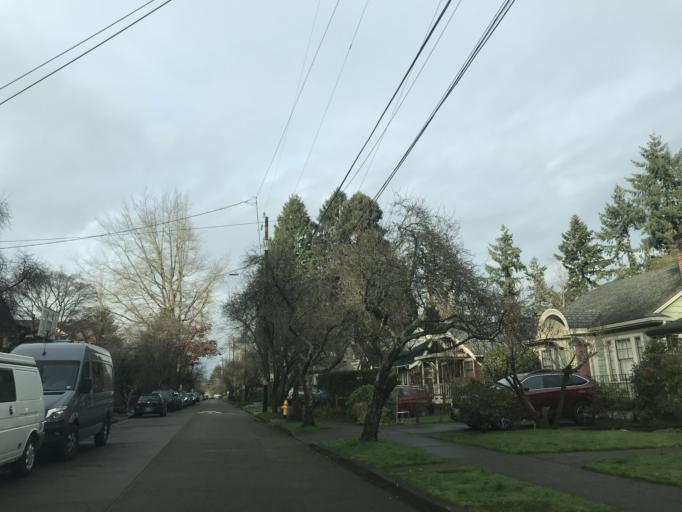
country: US
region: Washington
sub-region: King County
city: Seattle
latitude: 47.6366
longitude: -122.2994
